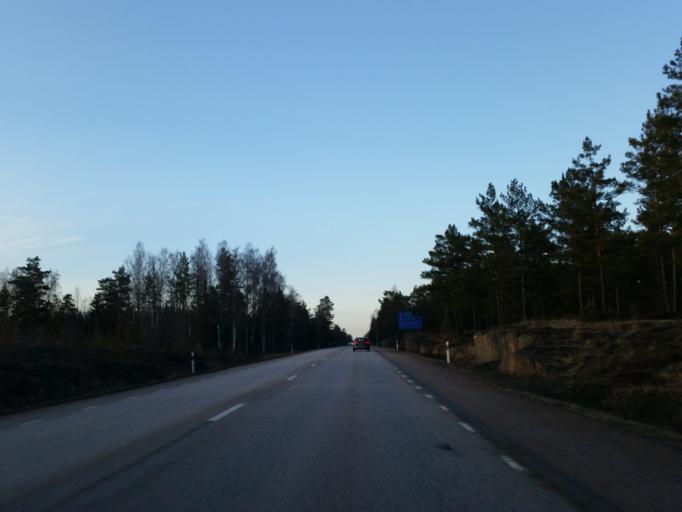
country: SE
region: Kalmar
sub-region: Oskarshamns Kommun
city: Oskarshamn
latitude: 57.4704
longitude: 16.5173
